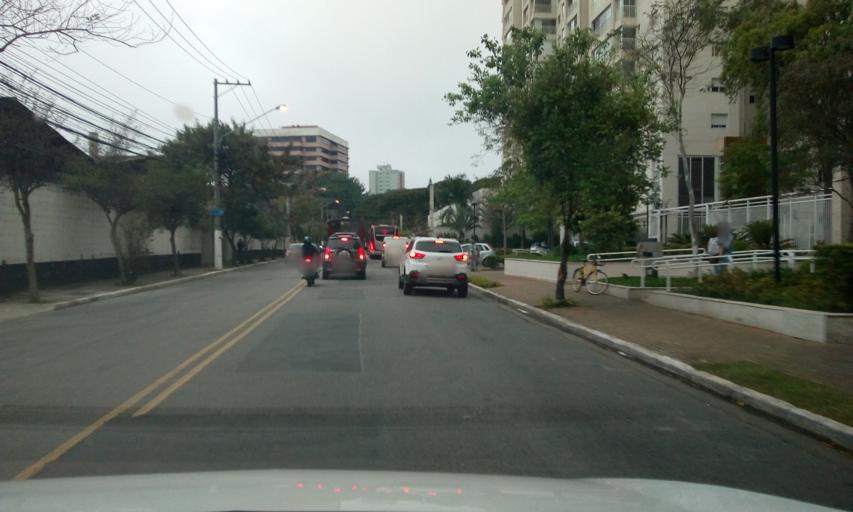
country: BR
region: Sao Paulo
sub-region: Taboao Da Serra
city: Taboao da Serra
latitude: -23.6511
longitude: -46.7182
